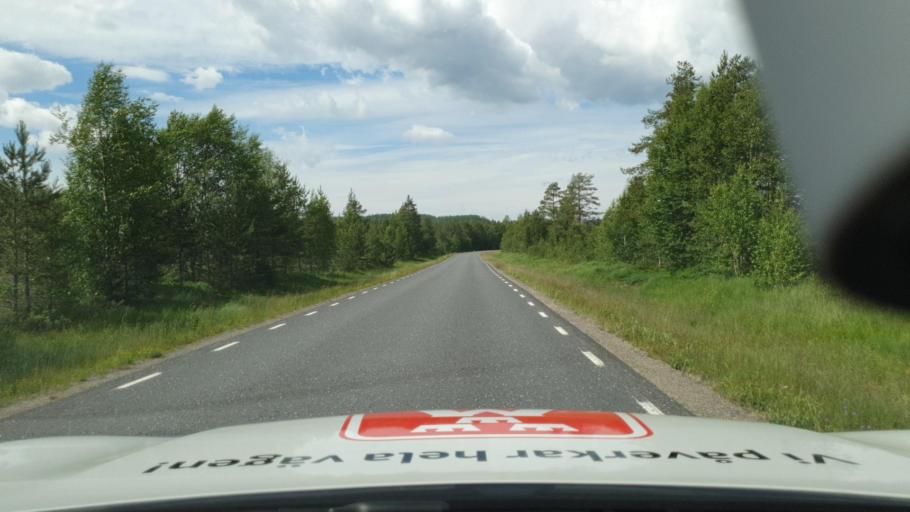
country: SE
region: Vaermland
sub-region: Torsby Kommun
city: Torsby
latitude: 60.6215
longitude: 12.7084
